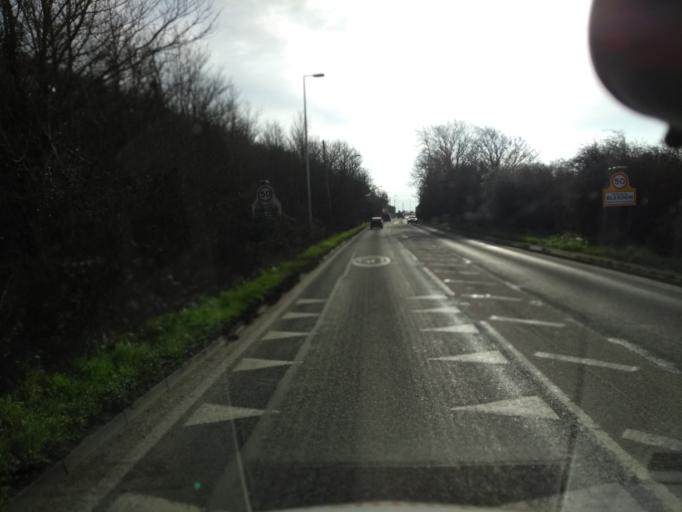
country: GB
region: England
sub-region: North Somerset
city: Bleadon
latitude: 51.3107
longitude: -2.9622
